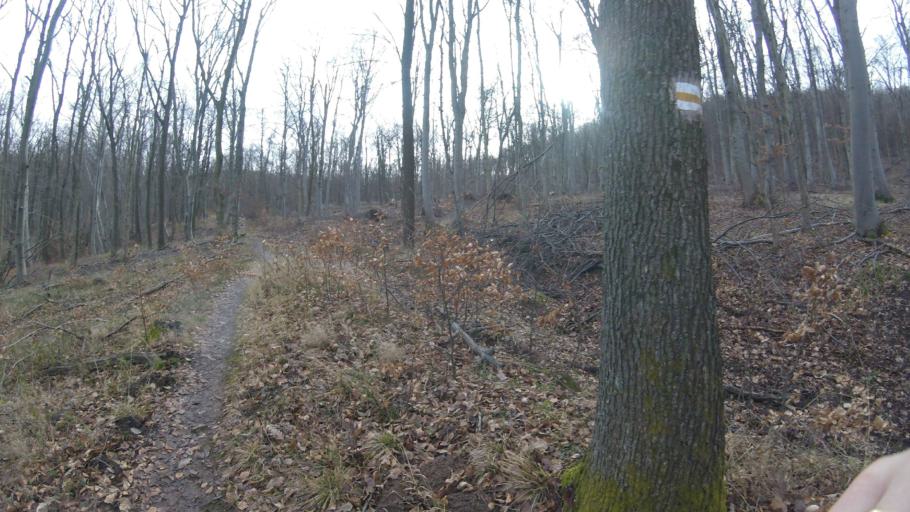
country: HU
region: Pest
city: Csobanka
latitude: 47.6957
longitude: 18.9718
